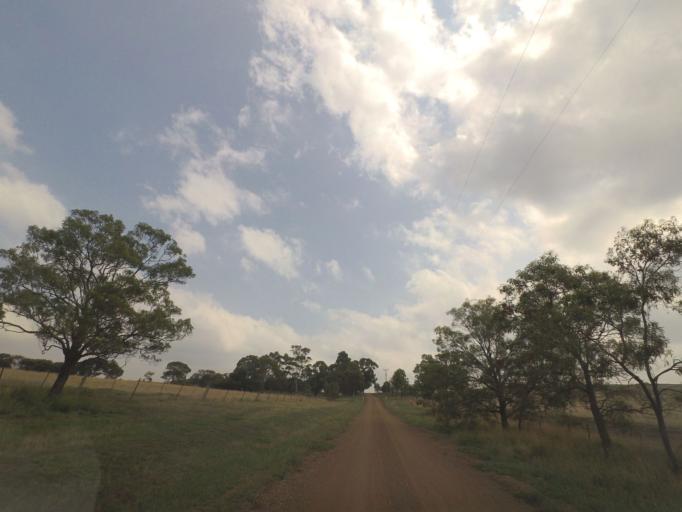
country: AU
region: Victoria
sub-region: Melton
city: Melton West
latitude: -37.6076
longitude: 144.5671
